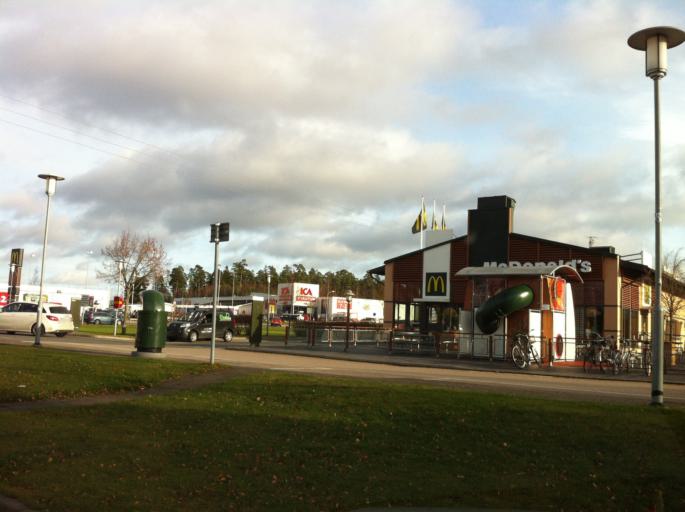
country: SE
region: Kronoberg
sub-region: Vaxjo Kommun
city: Vaexjoe
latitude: 56.8625
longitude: 14.7330
